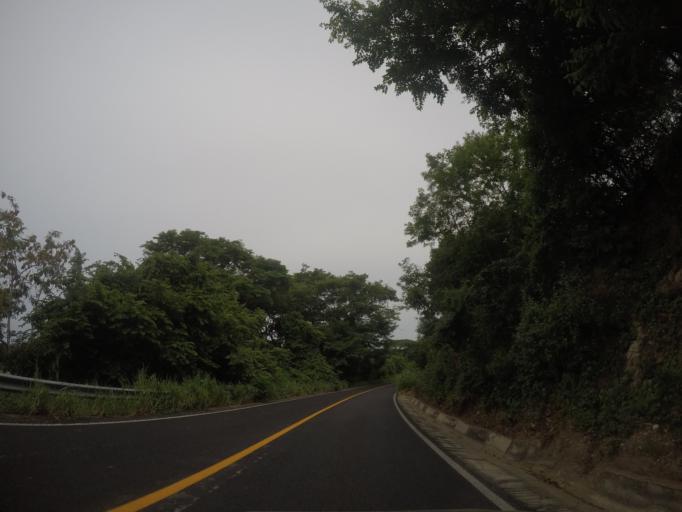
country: MX
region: Oaxaca
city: San Pedro Mixtepec
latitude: 15.9498
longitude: -97.2681
